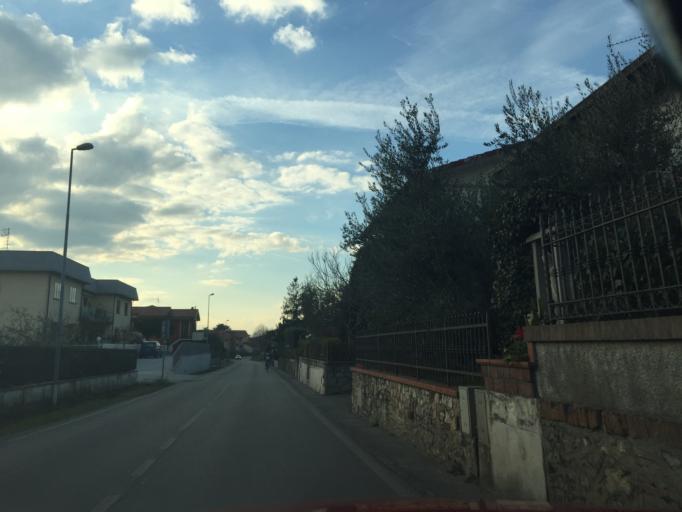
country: IT
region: Tuscany
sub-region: Provincia di Pistoia
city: Cintolese
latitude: 43.8599
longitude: 10.8261
